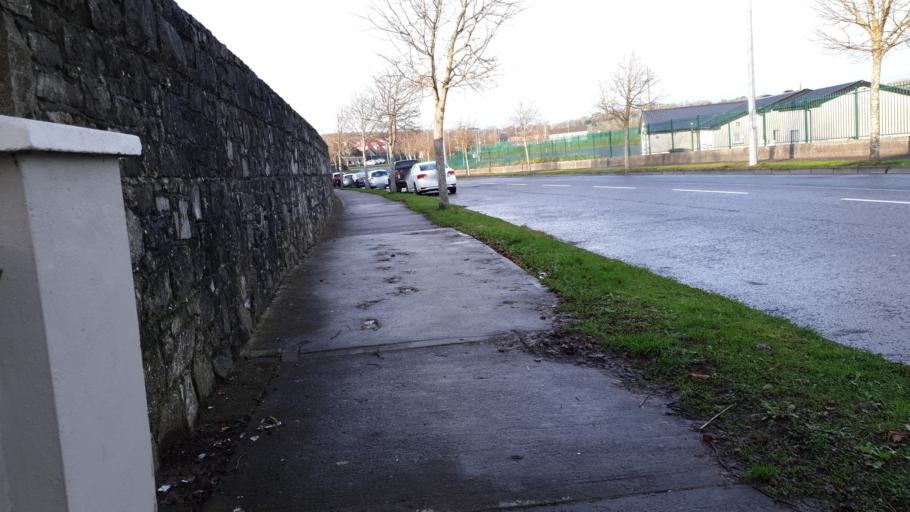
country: IE
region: Munster
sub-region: County Cork
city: Passage West
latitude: 51.8889
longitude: -8.3943
